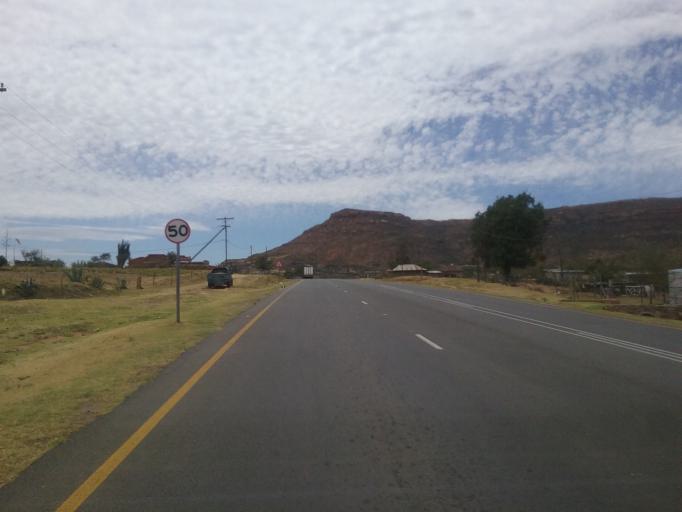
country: LS
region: Mafeteng
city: Mafeteng
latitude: -29.6456
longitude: 27.4672
